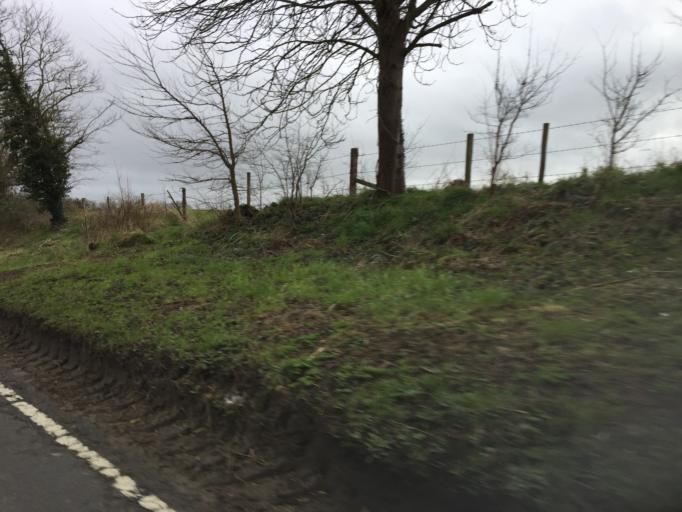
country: GB
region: England
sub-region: Oxfordshire
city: Faringdon
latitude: 51.6615
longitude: -1.5946
